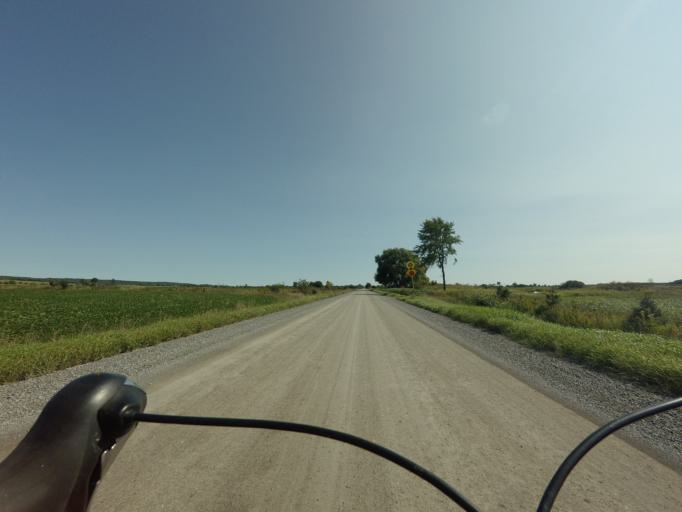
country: CA
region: Ontario
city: Arnprior
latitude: 45.3753
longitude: -76.1443
